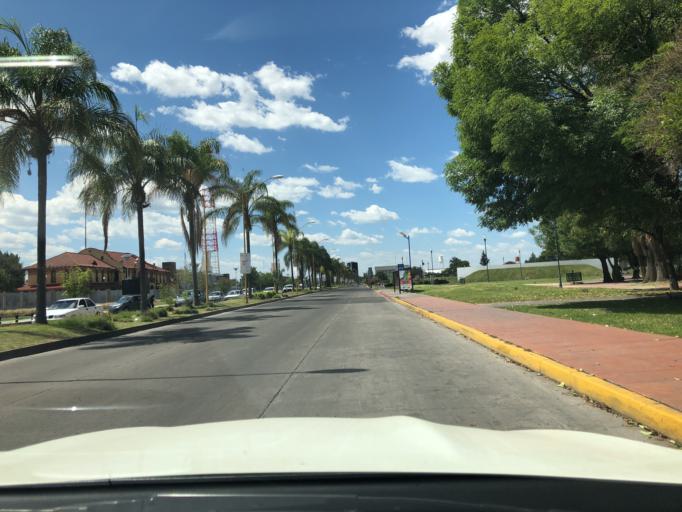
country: MX
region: Aguascalientes
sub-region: Aguascalientes
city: Aguascalientes
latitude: 21.8835
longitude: -102.2790
